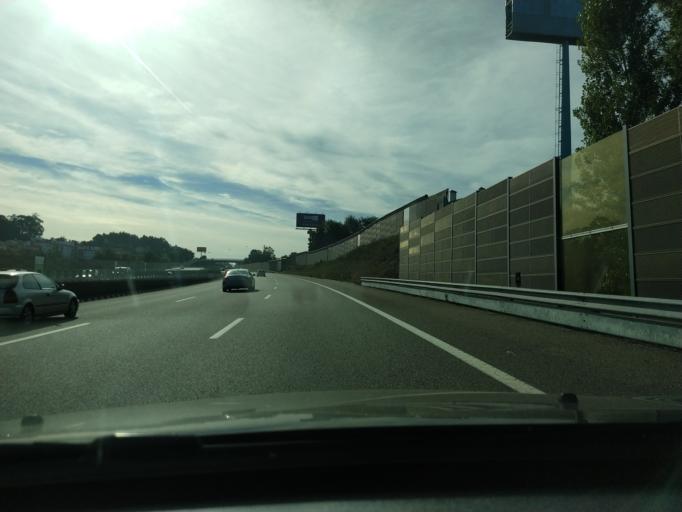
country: PT
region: Aveiro
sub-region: Santa Maria da Feira
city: Pacos de Brandao
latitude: 40.9761
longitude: -8.5757
